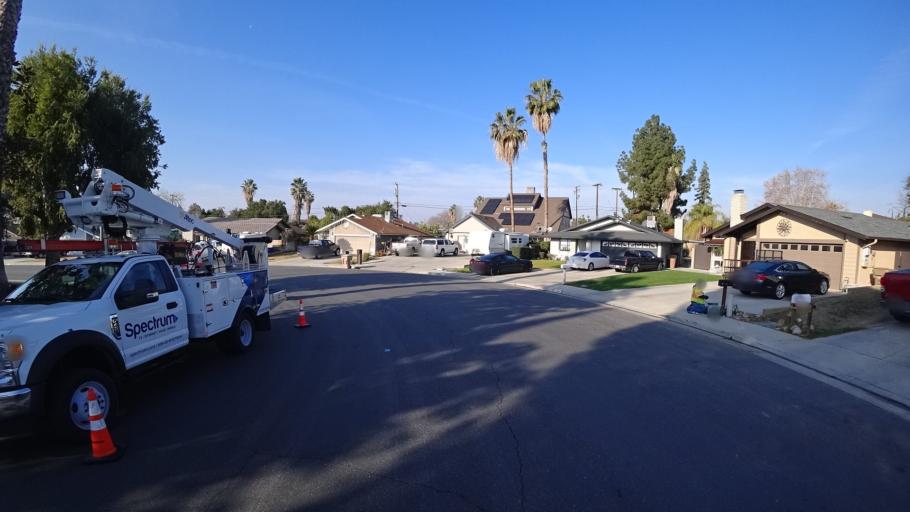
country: US
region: California
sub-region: Kern County
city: Oildale
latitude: 35.4011
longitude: -118.9446
